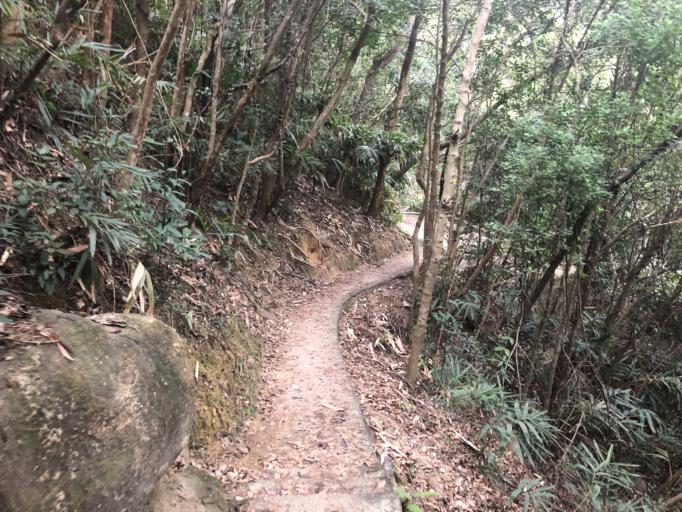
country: HK
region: Wanchai
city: Wan Chai
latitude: 22.2784
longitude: 114.2105
